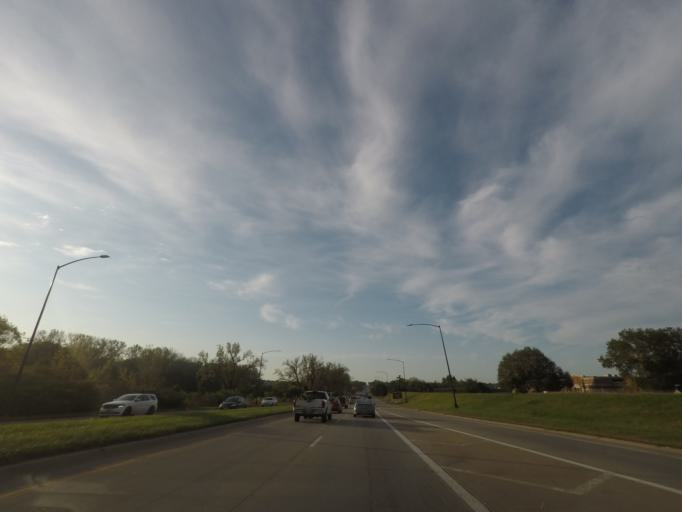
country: US
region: Iowa
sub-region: Polk County
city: Des Moines
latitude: 41.5787
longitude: -93.6450
